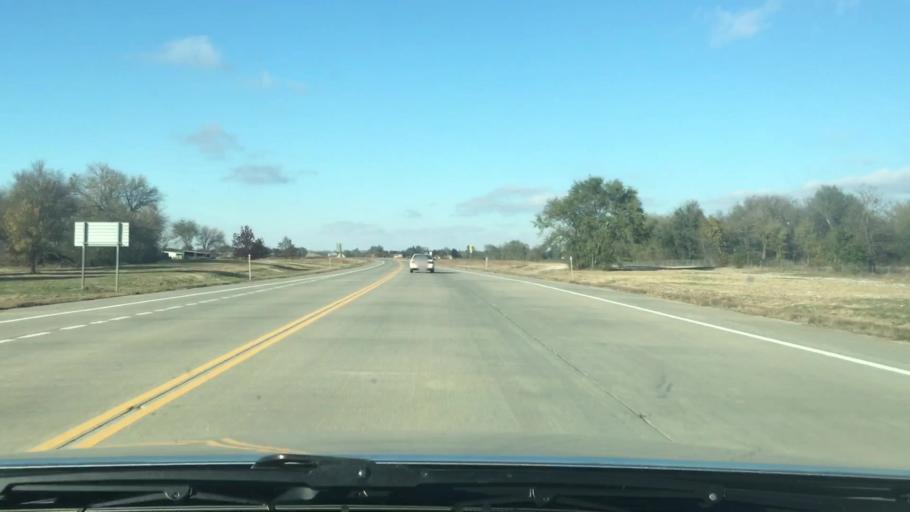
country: US
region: Kansas
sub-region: Reno County
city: Hutchinson
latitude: 38.0621
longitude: -97.9859
